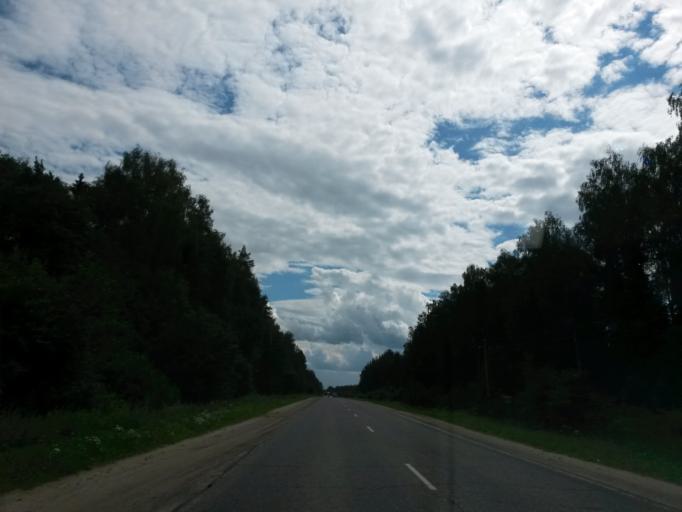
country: RU
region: Ivanovo
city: Novo-Talitsy
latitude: 57.0473
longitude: 40.7383
